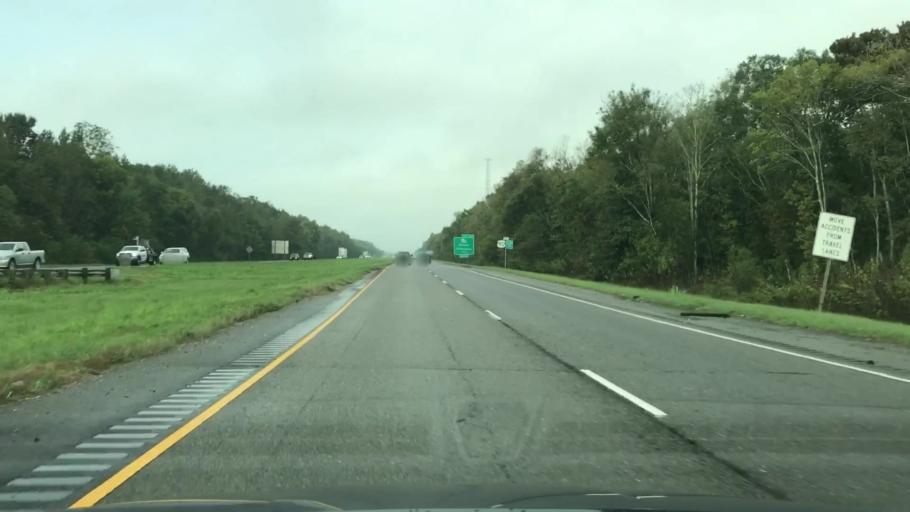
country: US
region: Louisiana
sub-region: Terrebonne Parish
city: Gray
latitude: 29.6819
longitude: -90.7605
